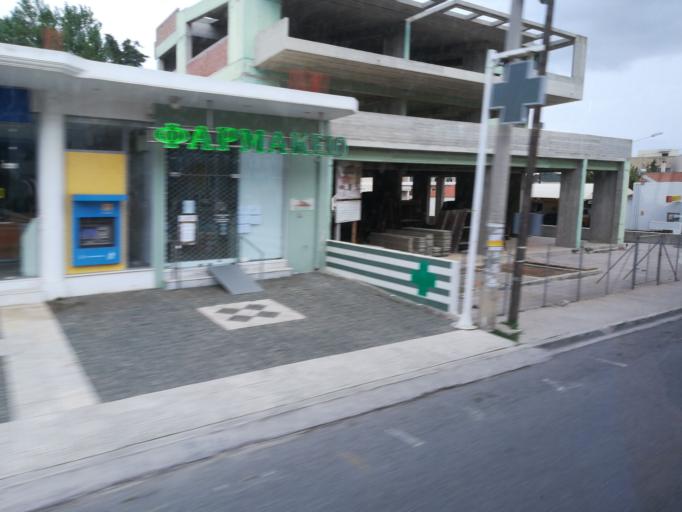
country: GR
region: Attica
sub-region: Nomarchia Anatolikis Attikis
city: Keratea
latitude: 37.8107
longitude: 23.9723
